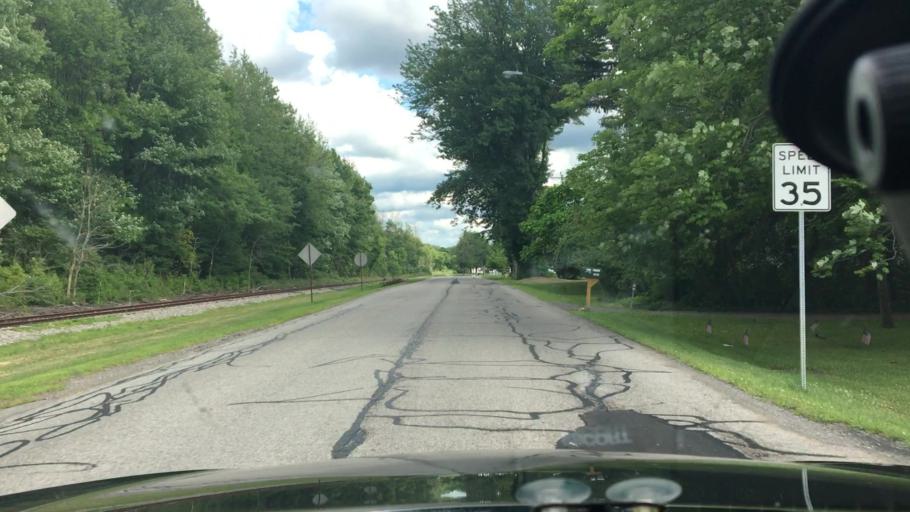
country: US
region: New York
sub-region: Erie County
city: Orchard Park
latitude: 42.7701
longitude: -78.7650
